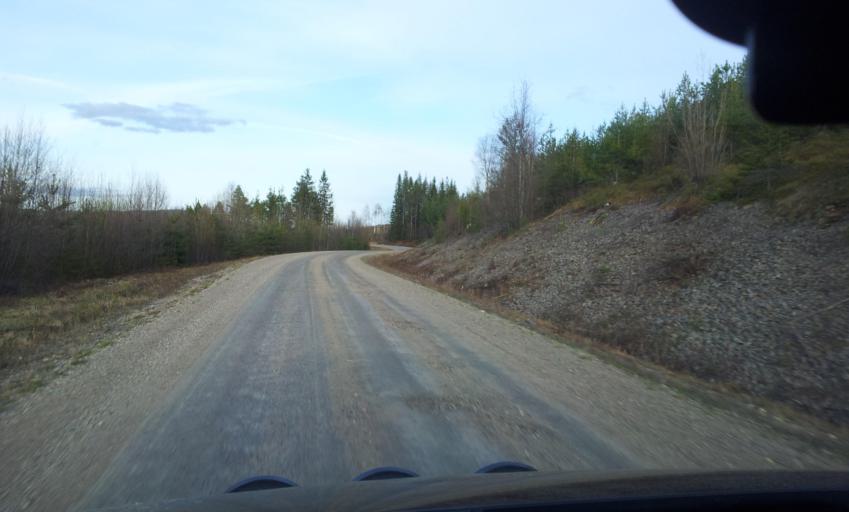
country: SE
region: Gaevleborg
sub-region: Ljusdals Kommun
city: Farila
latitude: 62.1132
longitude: 15.6983
